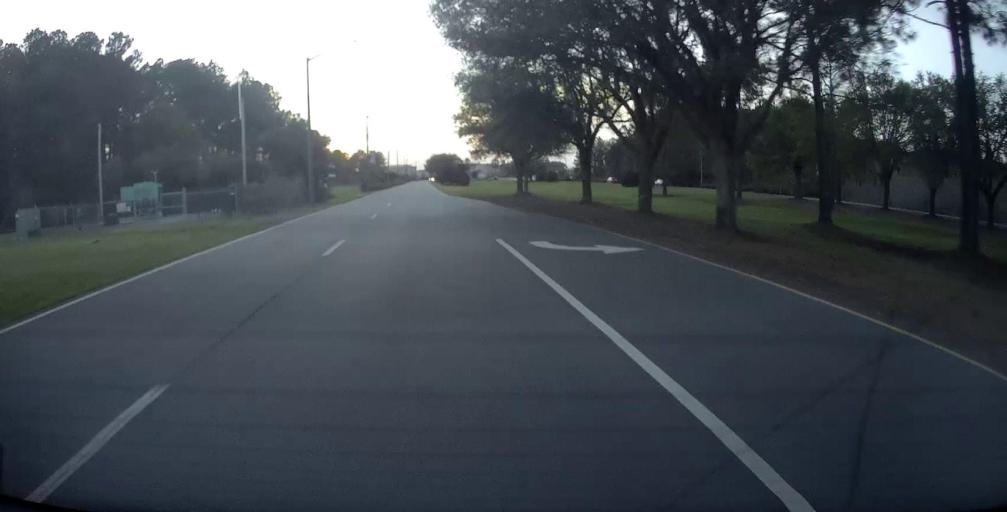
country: US
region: Georgia
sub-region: Chatham County
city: Pooler
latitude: 32.1378
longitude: -81.2271
